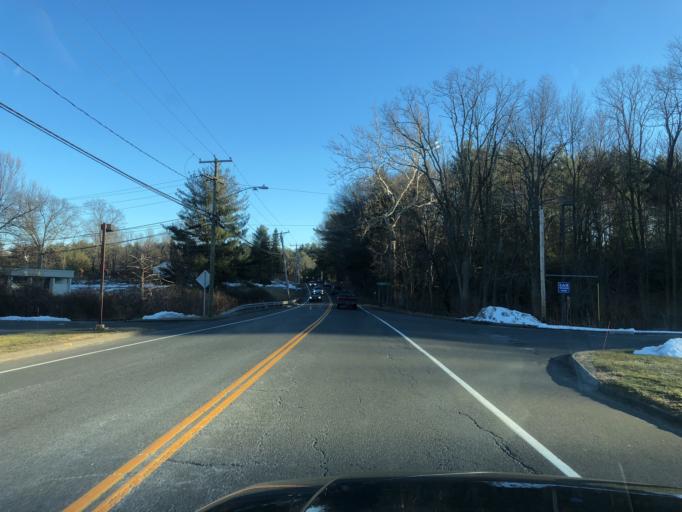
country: US
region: Connecticut
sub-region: Hartford County
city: Canton Valley
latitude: 41.8157
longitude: -72.8673
